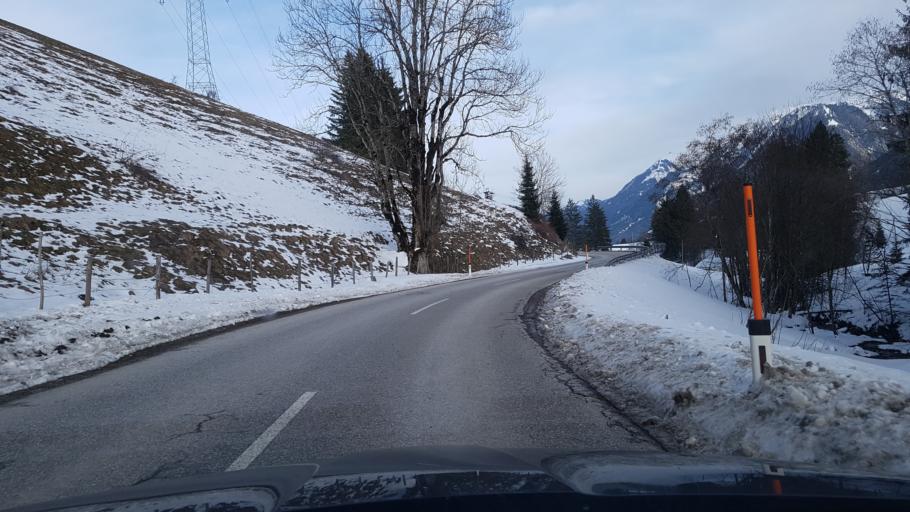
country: AT
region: Salzburg
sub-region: Politischer Bezirk Zell am See
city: Lend
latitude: 47.2950
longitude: 13.0166
